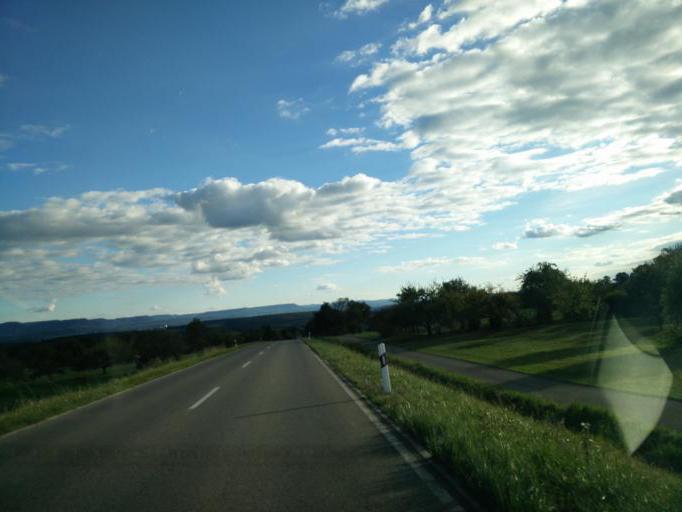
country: DE
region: Baden-Wuerttemberg
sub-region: Tuebingen Region
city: Kusterdingen
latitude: 48.5447
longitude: 9.0932
